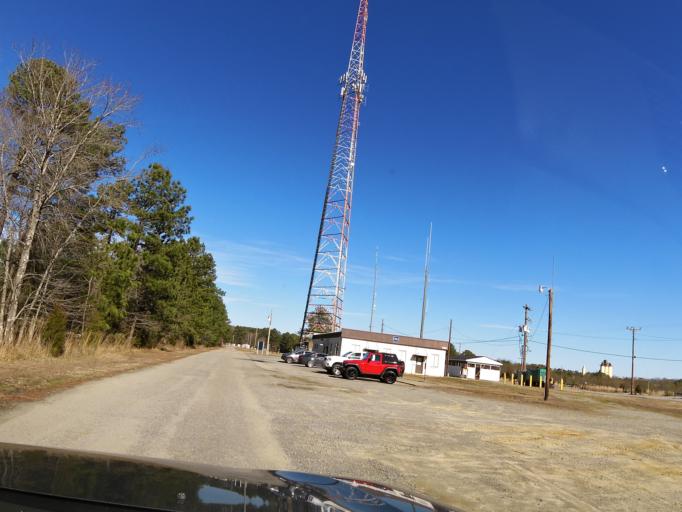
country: US
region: Virginia
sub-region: City of Petersburg
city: Petersburg
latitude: 37.1762
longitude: -77.4216
